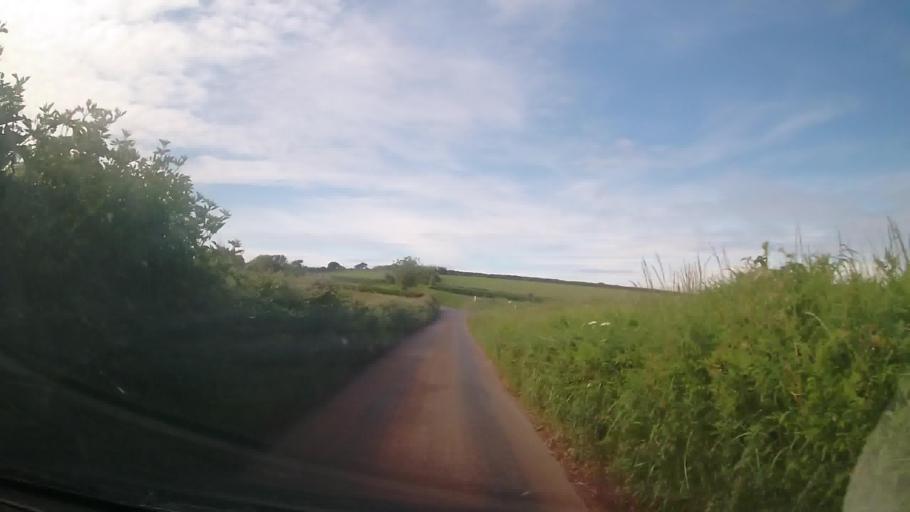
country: GB
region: England
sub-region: Devon
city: Salcombe
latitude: 50.2394
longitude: -3.6781
